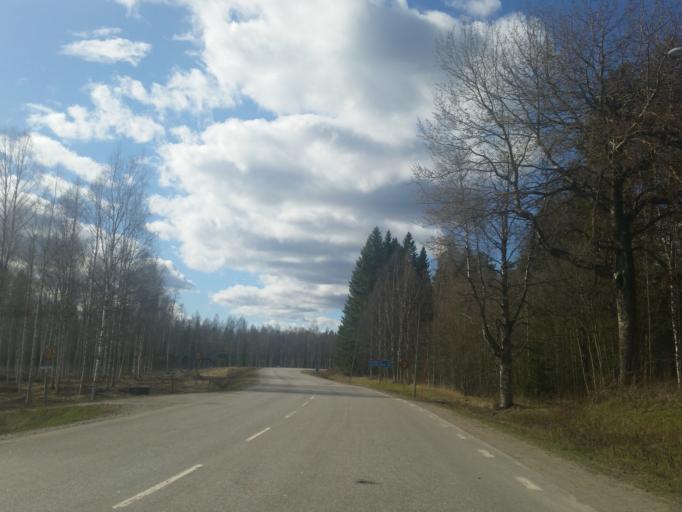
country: SE
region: Vaesterbotten
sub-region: Robertsfors Kommun
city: Robertsfors
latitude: 64.1967
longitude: 20.8406
